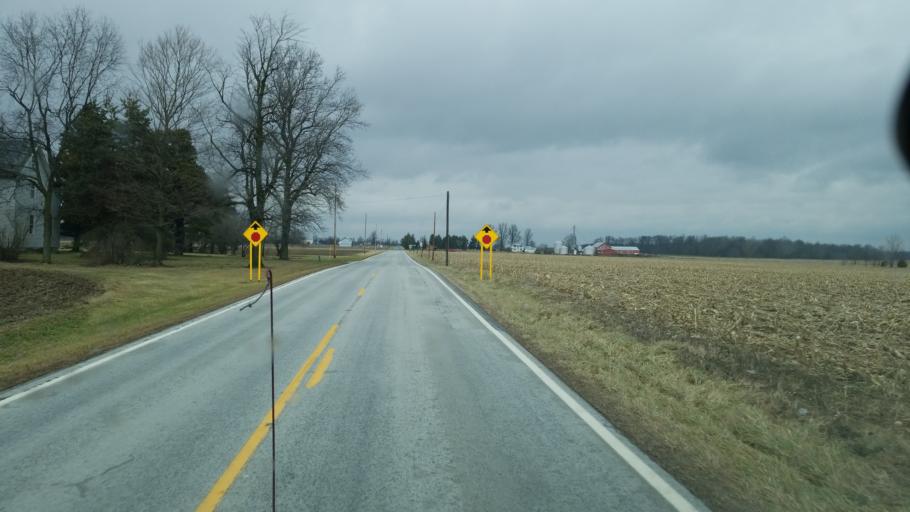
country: US
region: Ohio
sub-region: Hardin County
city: Forest
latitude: 40.8286
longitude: -83.4191
